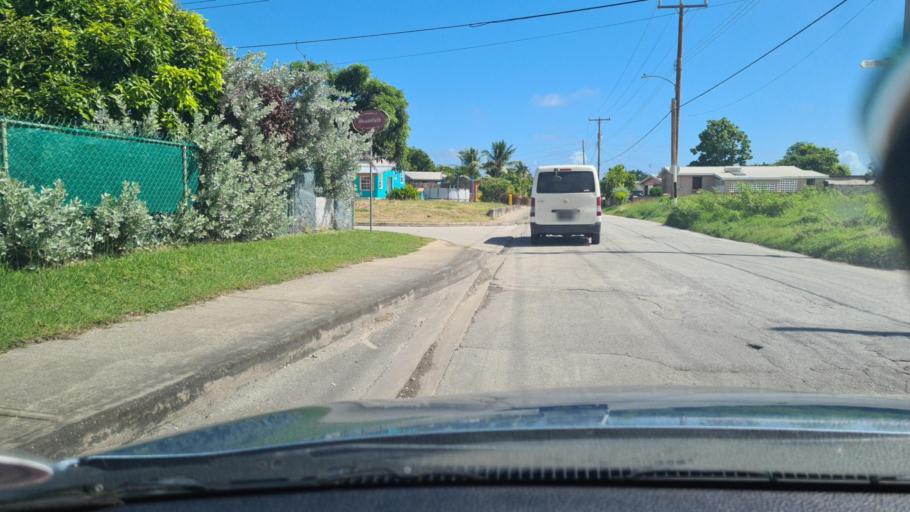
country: BB
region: Saint Philip
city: Crane
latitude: 13.1219
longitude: -59.4530
